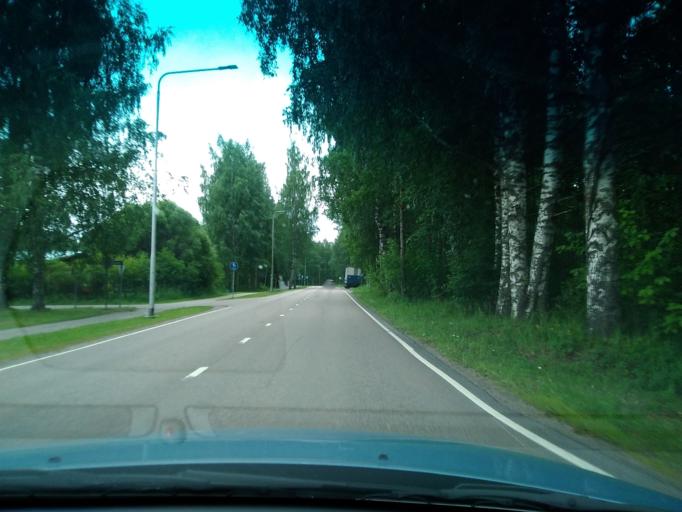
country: FI
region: Central Finland
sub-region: Keuruu
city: Multia
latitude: 62.4040
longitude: 24.7929
